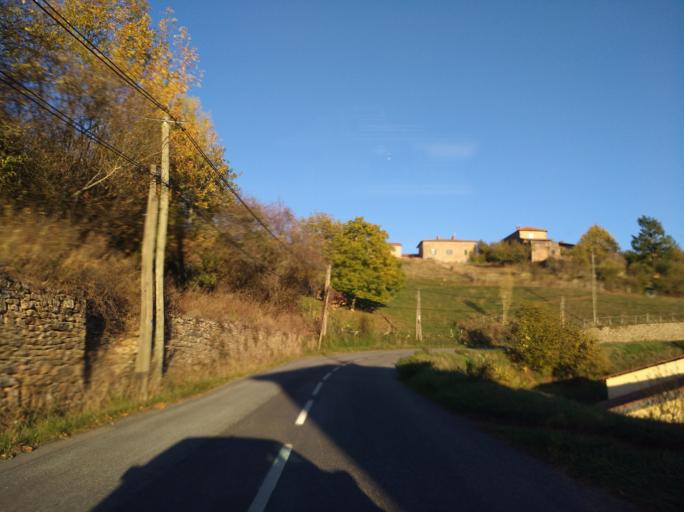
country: FR
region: Rhone-Alpes
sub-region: Departement du Rhone
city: Saint-Verand
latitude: 45.9615
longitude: 4.5630
